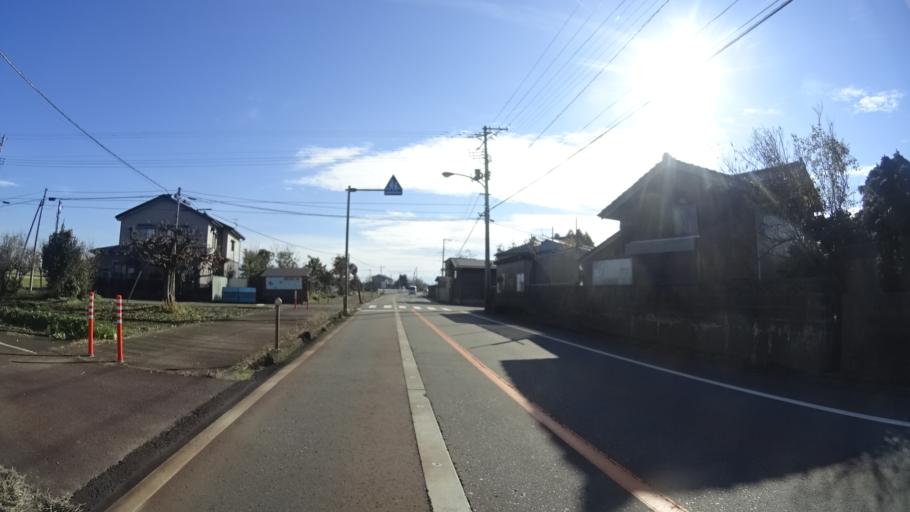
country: JP
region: Niigata
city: Mitsuke
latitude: 37.5518
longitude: 138.8661
